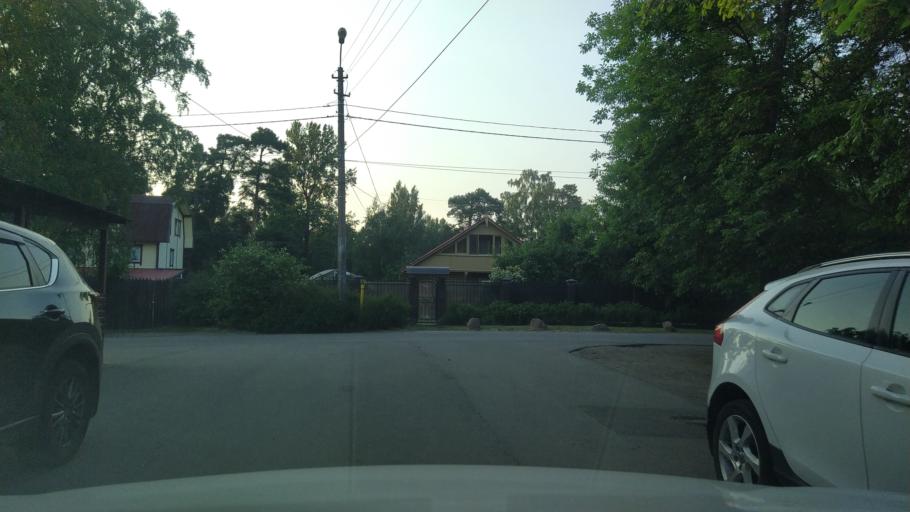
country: RU
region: St.-Petersburg
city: Sestroretsk
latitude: 60.0927
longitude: 29.9482
